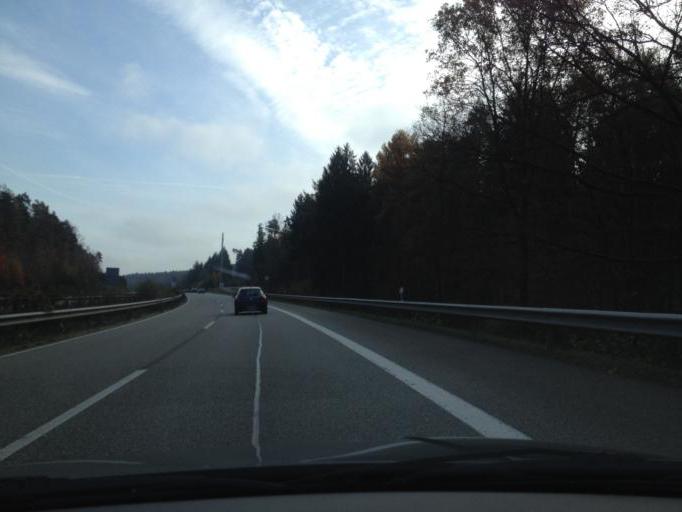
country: DE
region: Rheinland-Pfalz
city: Ruppertsweiler
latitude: 49.1985
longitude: 7.6994
